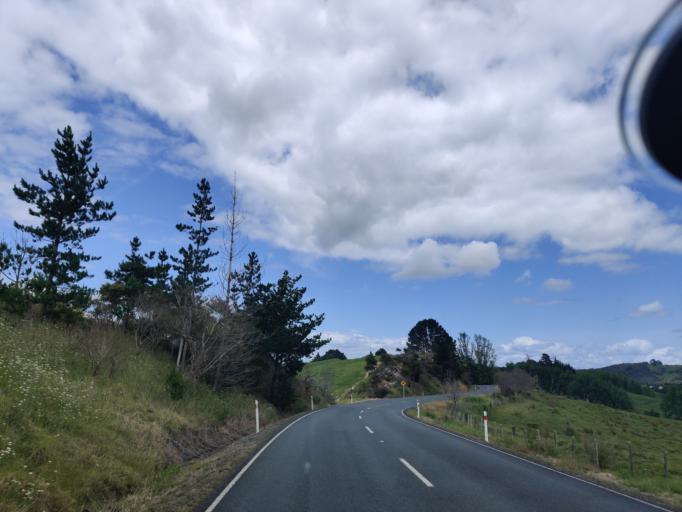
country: NZ
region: Northland
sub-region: Far North District
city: Kaitaia
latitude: -35.2780
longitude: 173.4837
